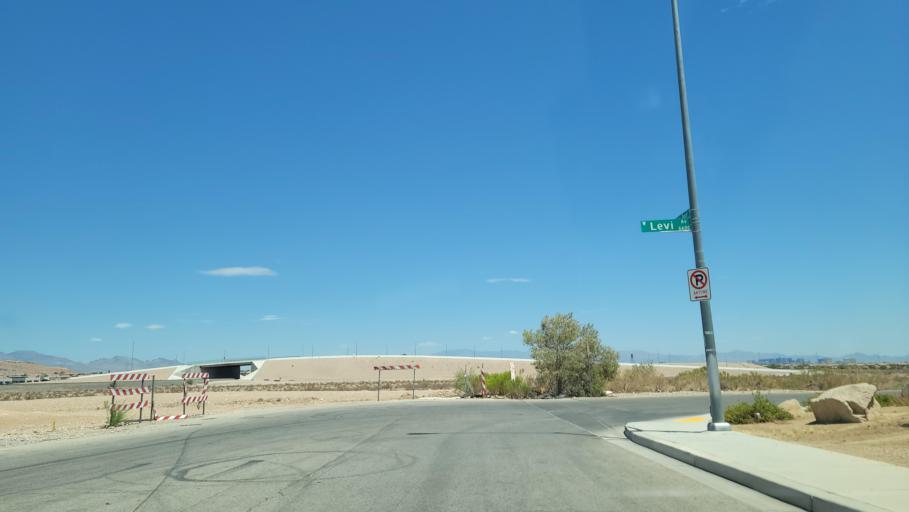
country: US
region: Nevada
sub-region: Clark County
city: Enterprise
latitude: 35.9947
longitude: -115.2397
